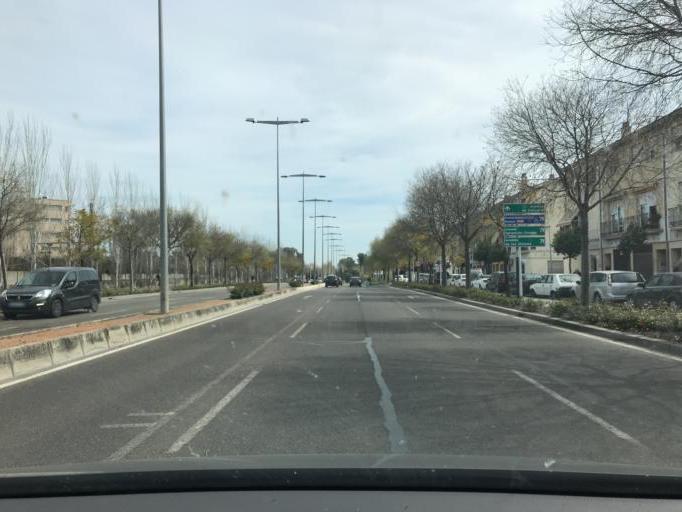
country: ES
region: Andalusia
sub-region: Province of Cordoba
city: Cordoba
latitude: 37.8965
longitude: -4.7711
